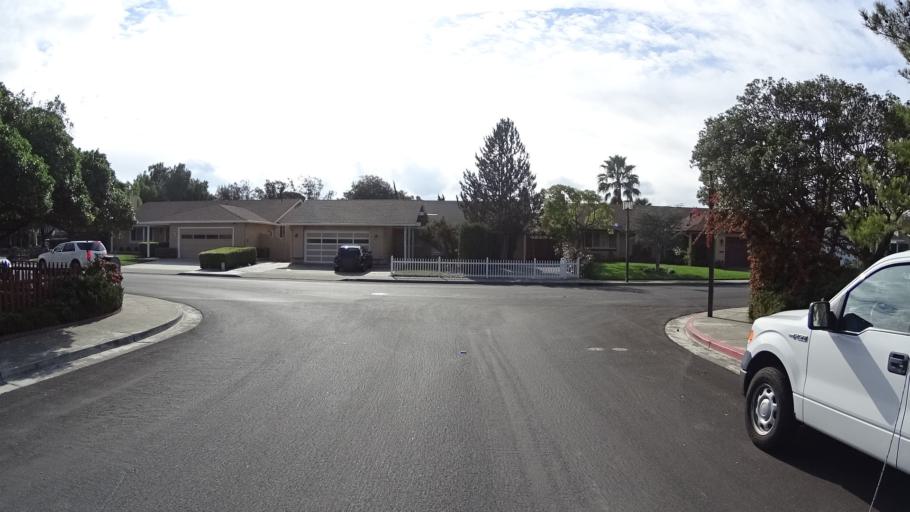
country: US
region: California
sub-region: San Mateo County
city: Redwood Shores
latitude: 37.5287
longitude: -122.2527
